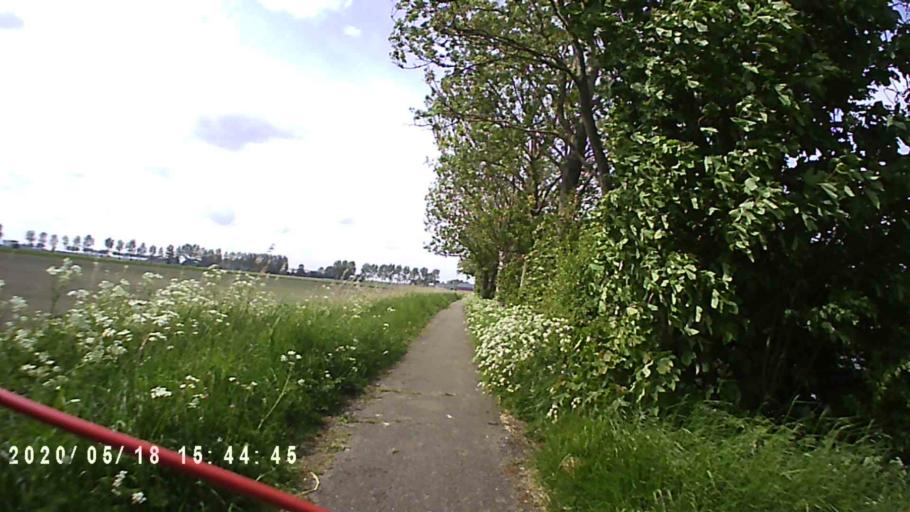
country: NL
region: Groningen
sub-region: Gemeente Winsum
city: Winsum
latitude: 53.3124
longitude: 6.4721
